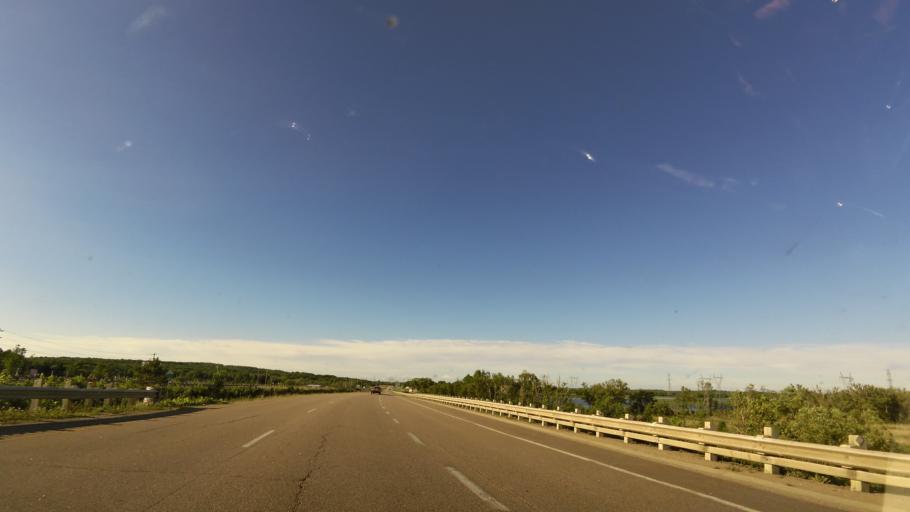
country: CA
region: Ontario
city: Midland
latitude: 44.7532
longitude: -79.7028
